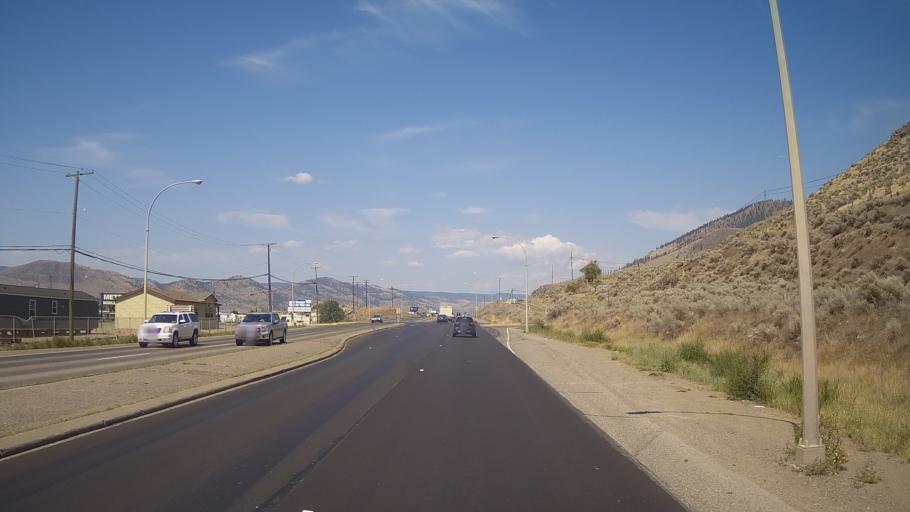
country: CA
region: British Columbia
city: Kamloops
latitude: 50.6969
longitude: -120.3243
